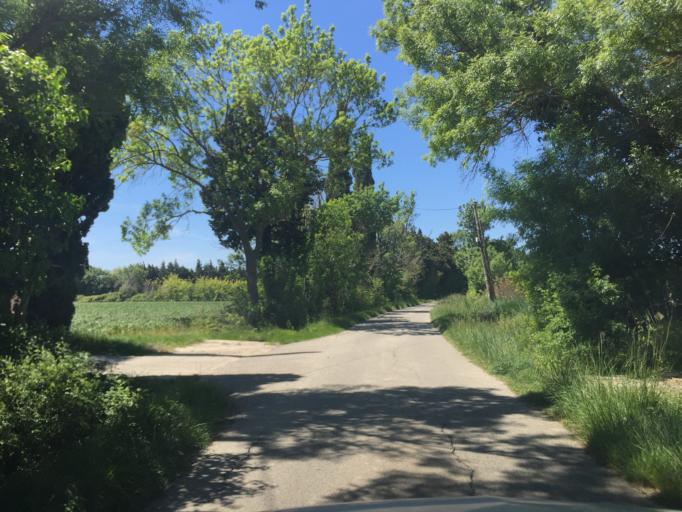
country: FR
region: Provence-Alpes-Cote d'Azur
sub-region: Departement du Vaucluse
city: Caderousse
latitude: 44.1020
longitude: 4.7661
